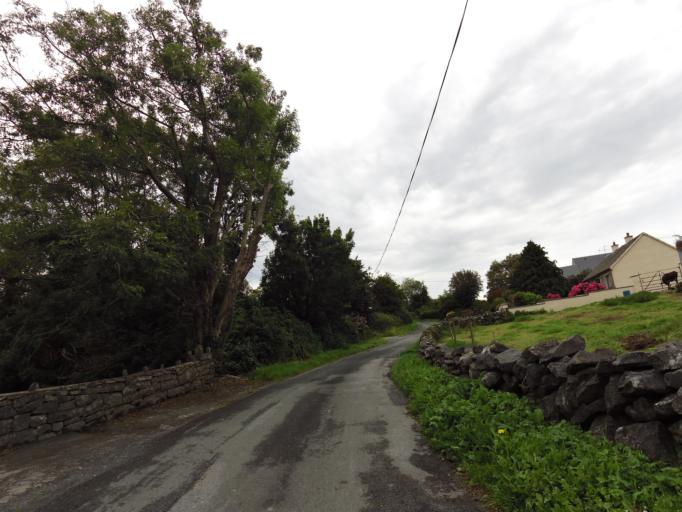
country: IE
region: Connaught
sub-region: County Galway
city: Gaillimh
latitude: 53.3016
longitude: -9.0734
